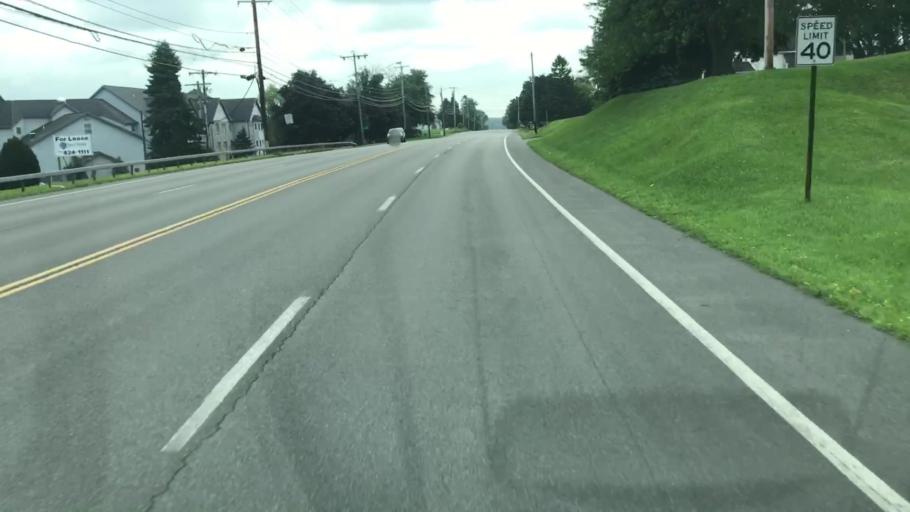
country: US
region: New York
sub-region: Onondaga County
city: Galeville
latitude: 43.0983
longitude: -76.1802
